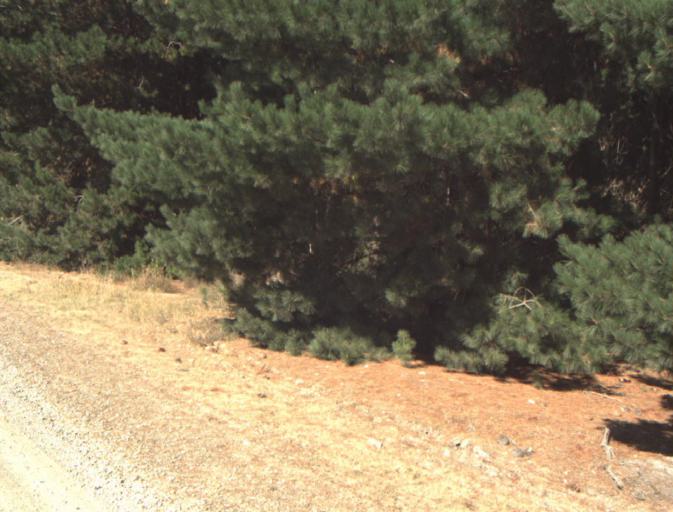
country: AU
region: Tasmania
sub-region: Launceston
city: Mayfield
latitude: -41.1654
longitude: 147.2123
